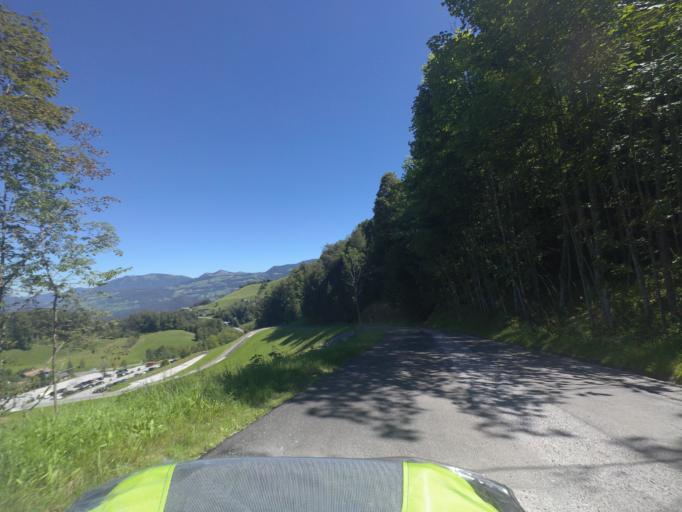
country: AT
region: Salzburg
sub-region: Politischer Bezirk Hallein
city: Hallein
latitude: 47.6574
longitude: 13.0923
